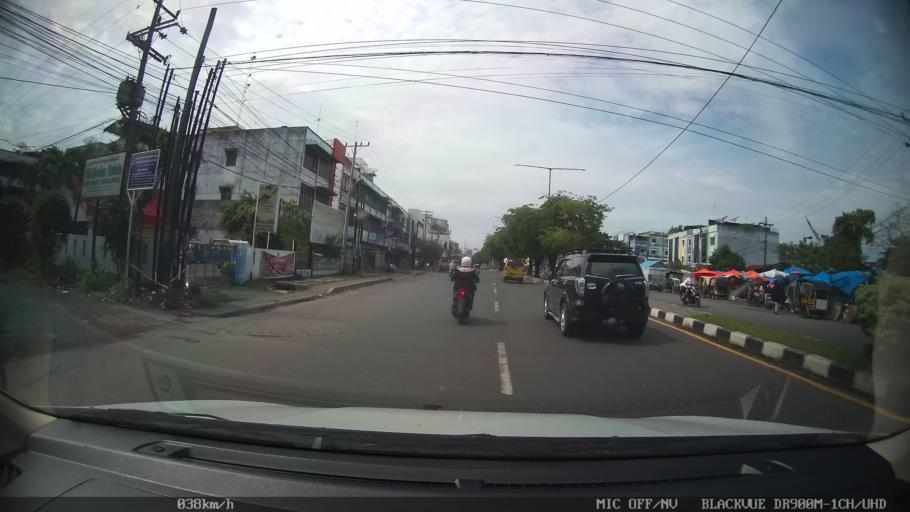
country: ID
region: North Sumatra
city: Medan
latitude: 3.5989
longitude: 98.7065
